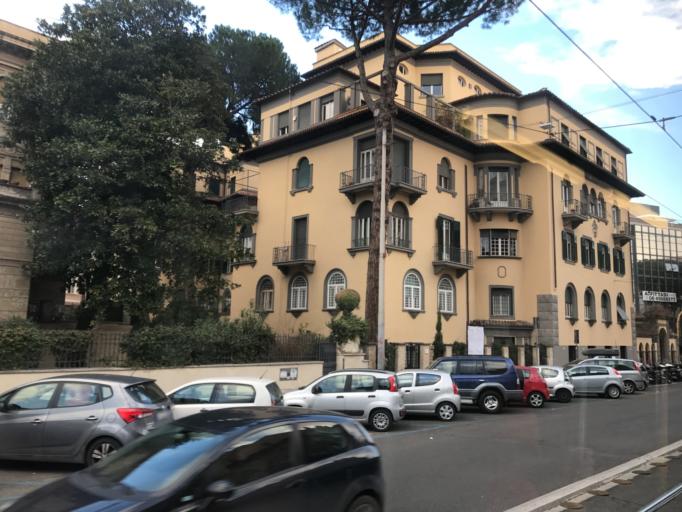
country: IT
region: Latium
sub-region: Citta metropolitana di Roma Capitale
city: Rome
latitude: 41.9103
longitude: 12.5100
